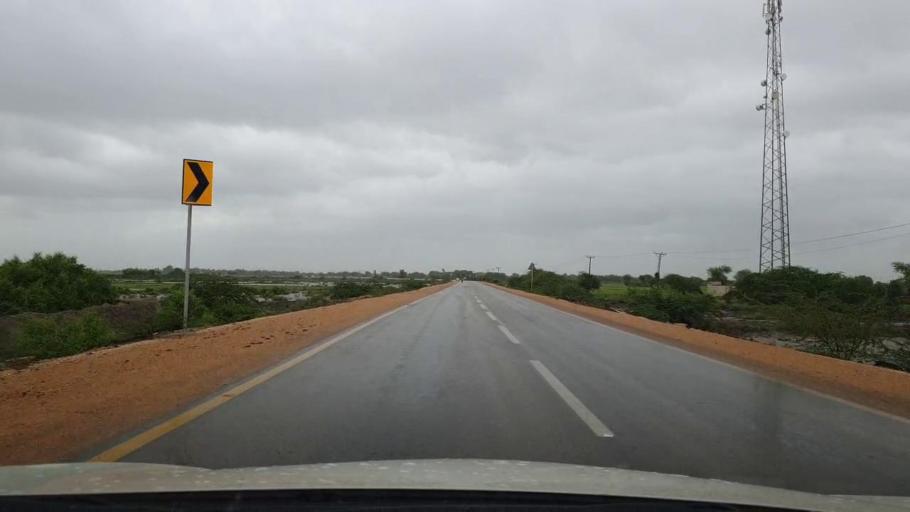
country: PK
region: Sindh
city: Kario
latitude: 24.6537
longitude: 68.6653
